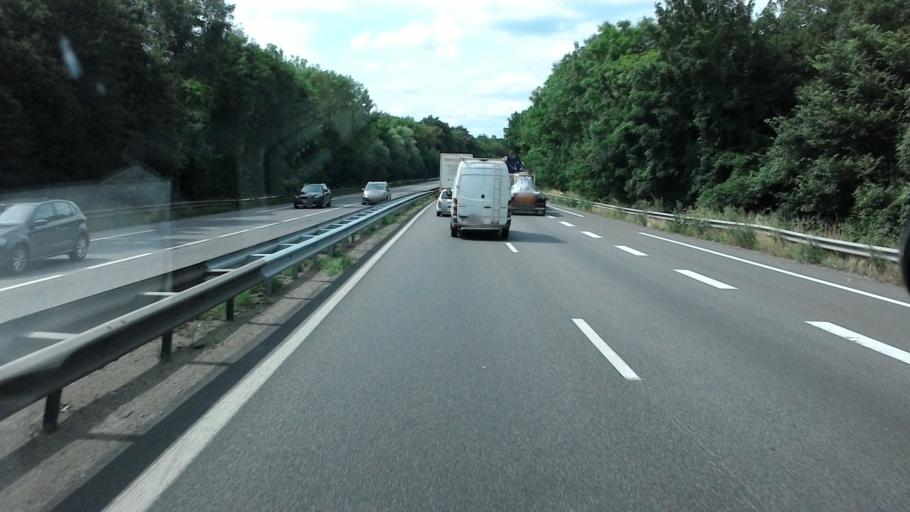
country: FR
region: Lorraine
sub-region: Departement de Meurthe-et-Moselle
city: Chavigny
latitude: 48.6484
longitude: 6.1355
